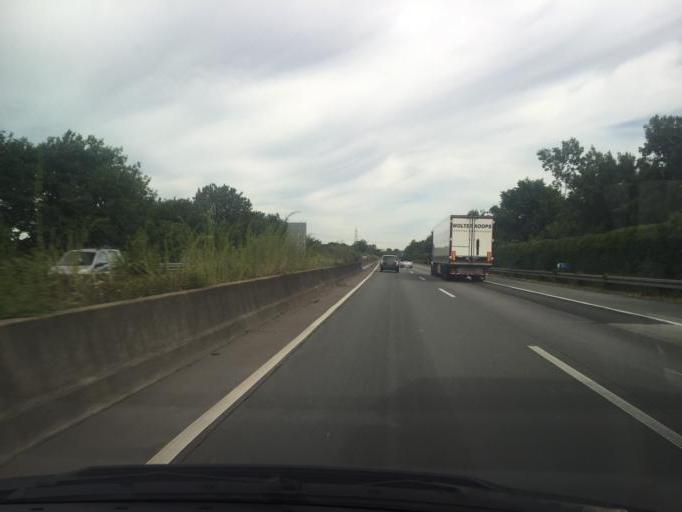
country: DE
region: North Rhine-Westphalia
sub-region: Regierungsbezirk Dusseldorf
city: Moers
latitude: 51.4450
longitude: 6.5994
